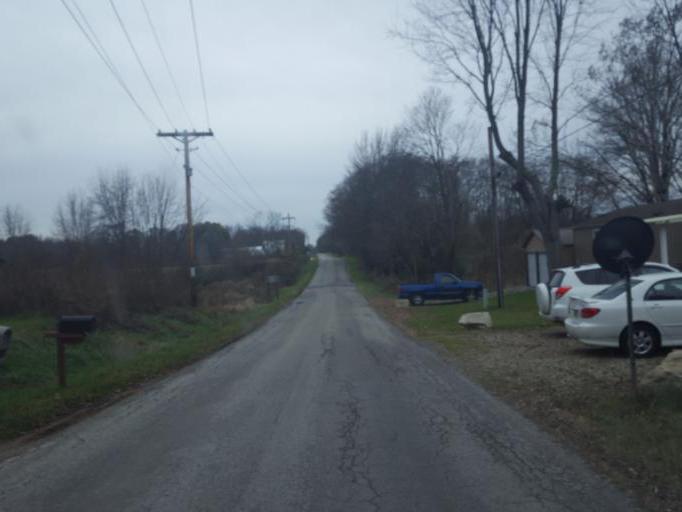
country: US
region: Ohio
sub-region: Delaware County
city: Ashley
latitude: 40.4321
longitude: -82.9822
